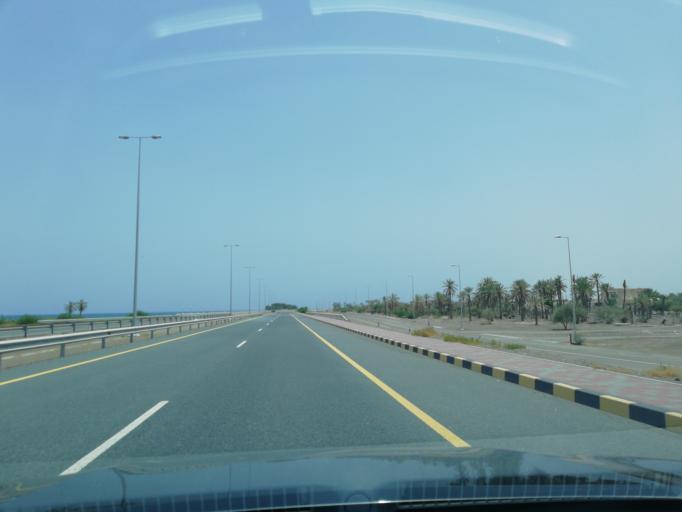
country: OM
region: Al Batinah
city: Shinas
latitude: 24.8328
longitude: 56.4296
